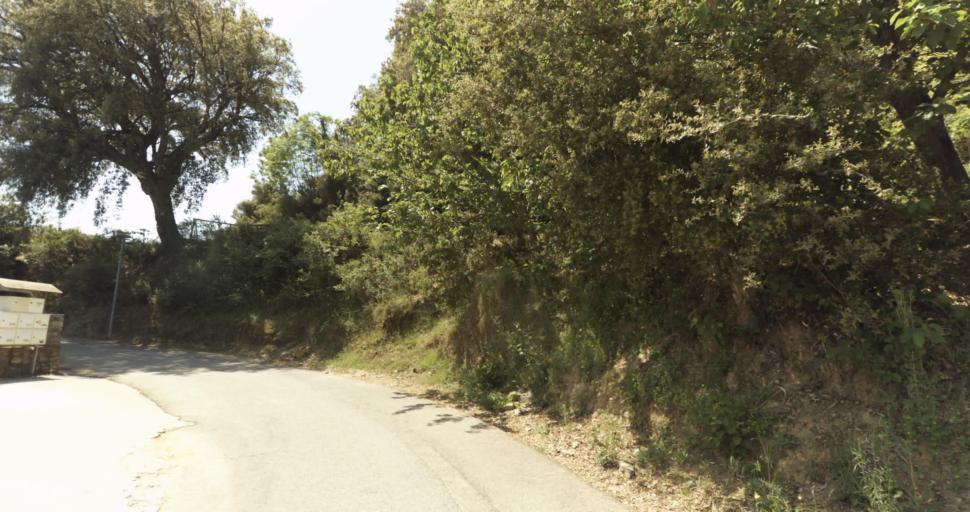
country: FR
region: Corsica
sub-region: Departement de la Haute-Corse
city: Biguglia
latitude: 42.5943
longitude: 9.4258
